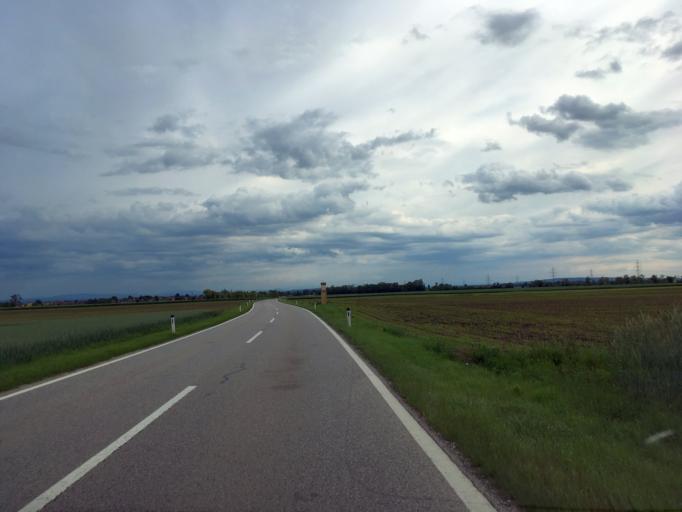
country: AT
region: Lower Austria
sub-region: Politischer Bezirk Tulln
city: Kirchberg am Wagram
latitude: 48.4198
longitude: 15.8941
